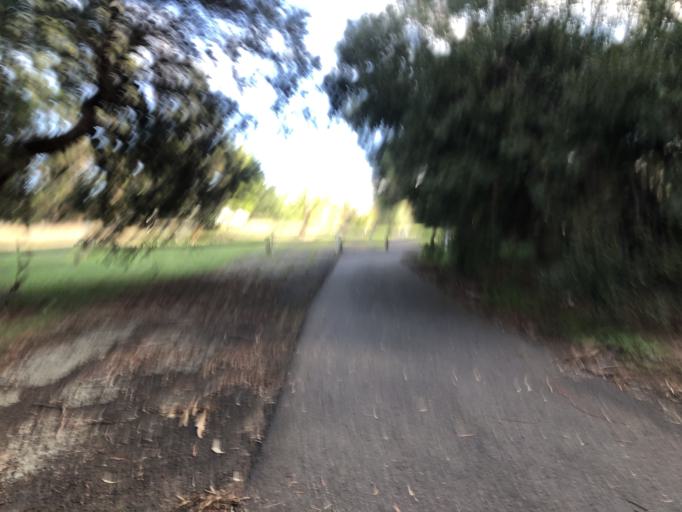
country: AU
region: New South Wales
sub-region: Orange Municipality
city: Orange
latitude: -33.3236
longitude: 149.0861
